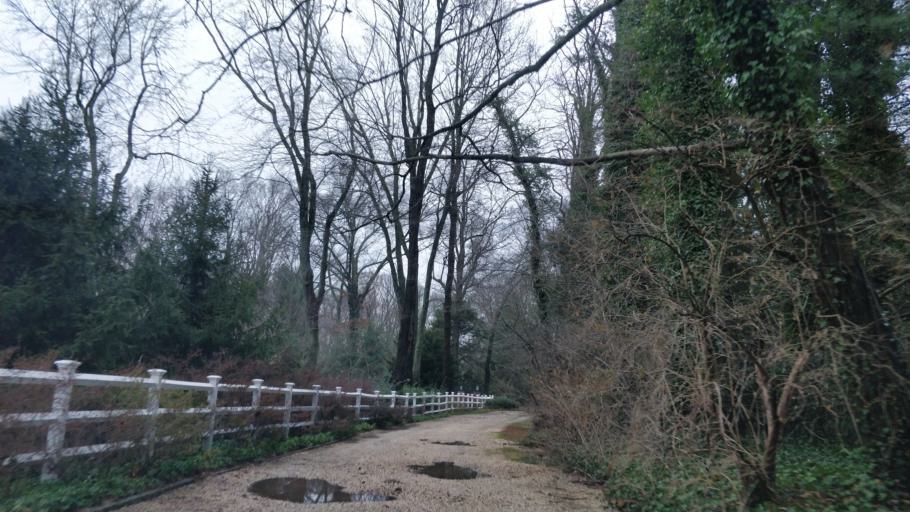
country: US
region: New York
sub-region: Nassau County
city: Upper Brookville
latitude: 40.8598
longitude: -73.5725
